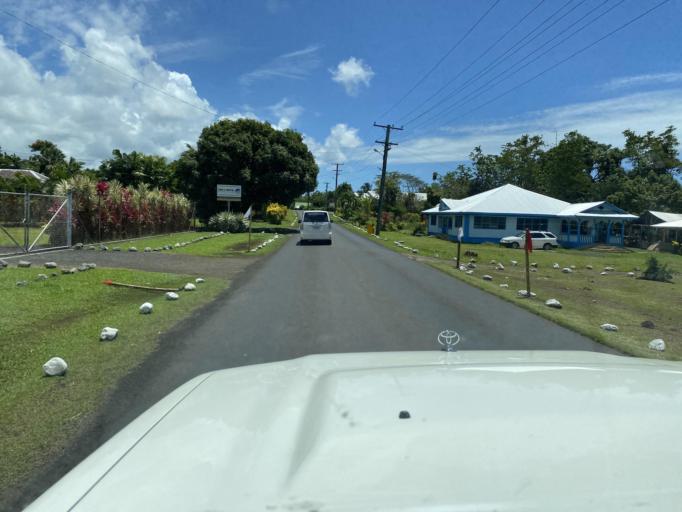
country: WS
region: Tuamasaga
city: Vaiusu
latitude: -13.8499
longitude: -171.7853
